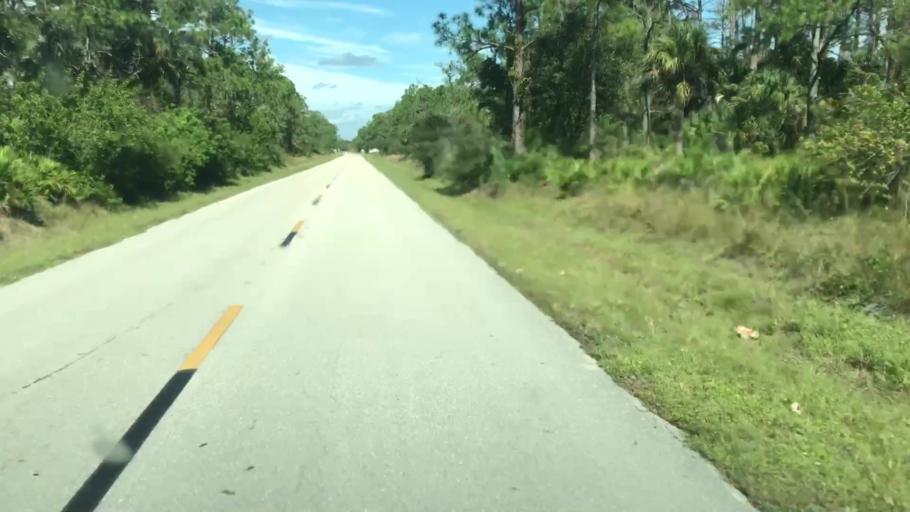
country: US
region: Florida
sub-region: Lee County
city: Lehigh Acres
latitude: 26.6546
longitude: -81.6464
